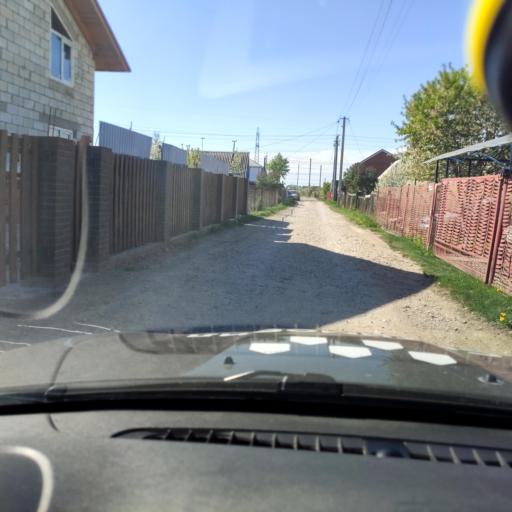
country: RU
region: Samara
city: Tol'yatti
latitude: 53.5931
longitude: 49.2892
